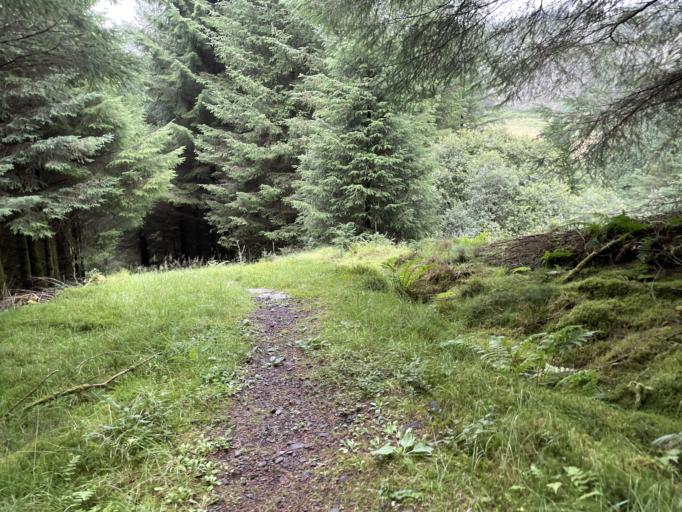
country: GB
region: Scotland
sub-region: South Ayrshire
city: Maybole
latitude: 55.2043
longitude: -4.6737
